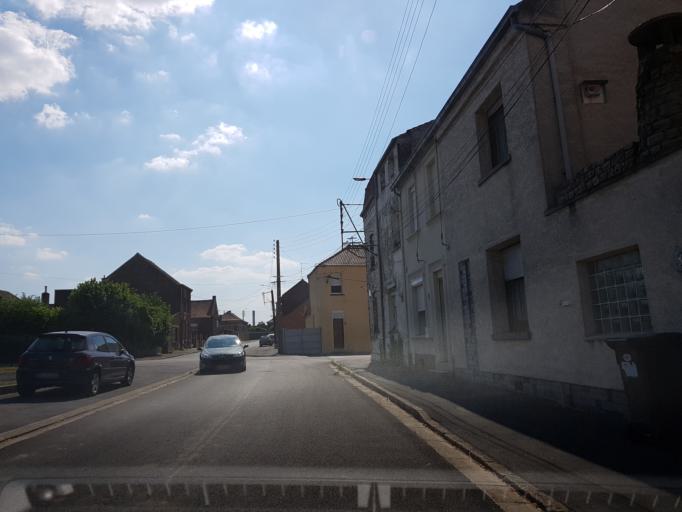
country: FR
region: Nord-Pas-de-Calais
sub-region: Departement du Nord
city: Roeulx
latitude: 50.3078
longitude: 3.3379
